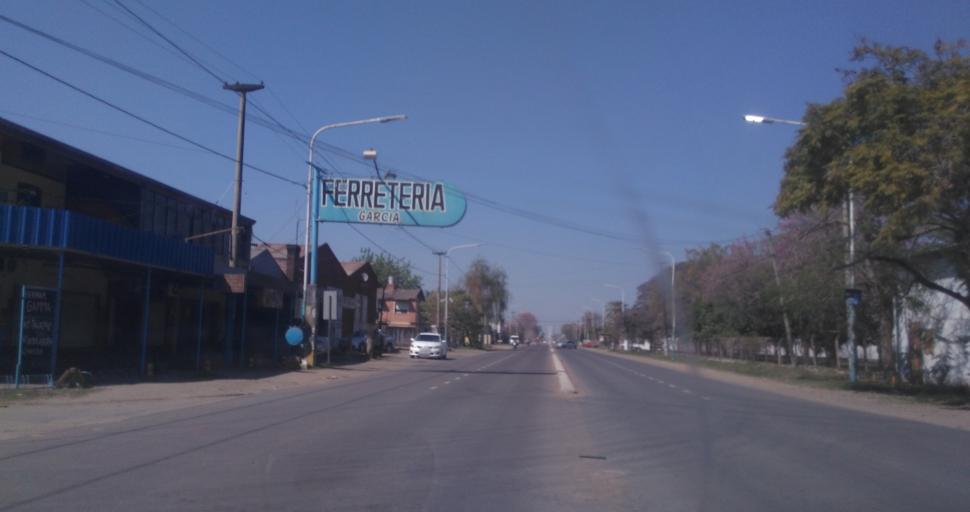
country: AR
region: Chaco
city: Fontana
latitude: -27.4286
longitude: -59.0264
